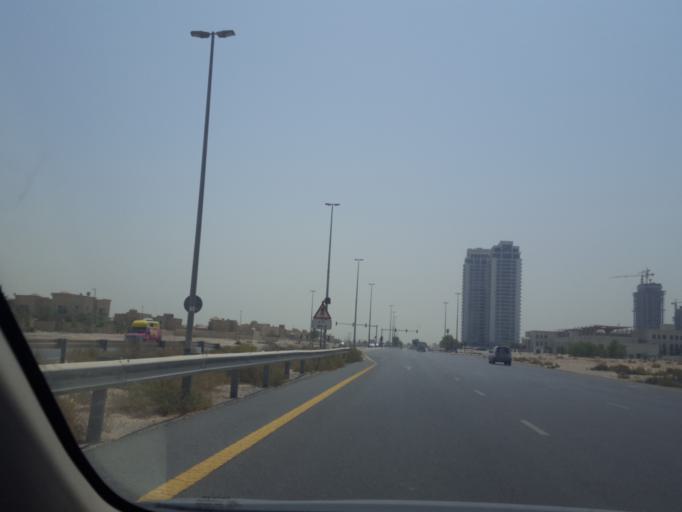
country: AE
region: Dubai
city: Dubai
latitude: 25.0806
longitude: 55.2383
